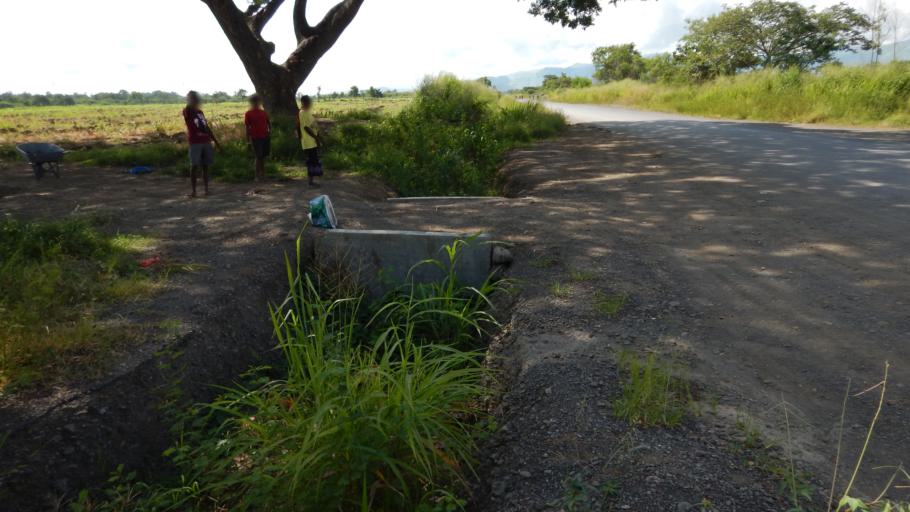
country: PG
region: Eastern Highlands
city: Kainantu
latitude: -6.2962
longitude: 146.2202
